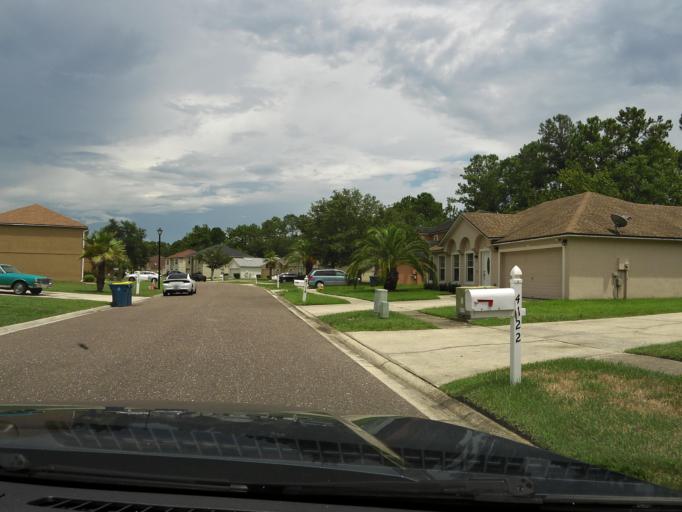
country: US
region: Florida
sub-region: Duval County
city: Jacksonville
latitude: 30.4228
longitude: -81.7217
